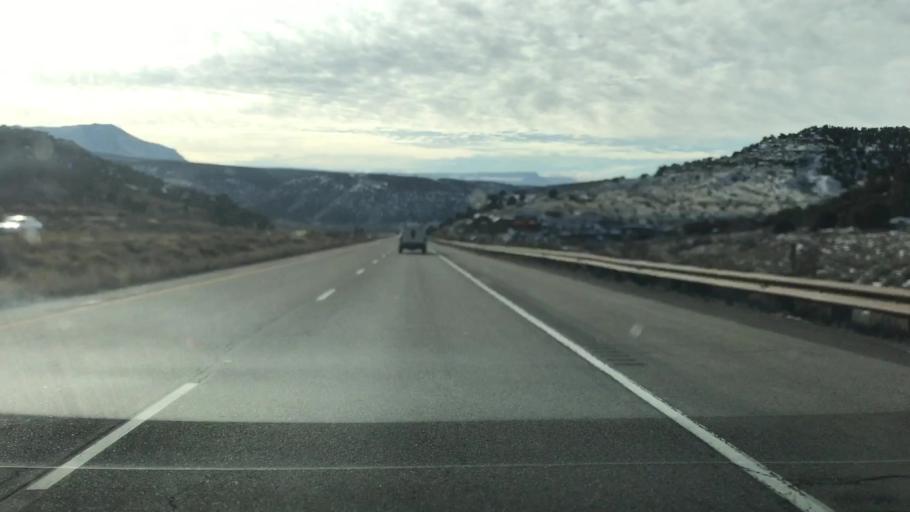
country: US
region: Colorado
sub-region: Garfield County
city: Parachute
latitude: 39.3669
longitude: -108.1704
